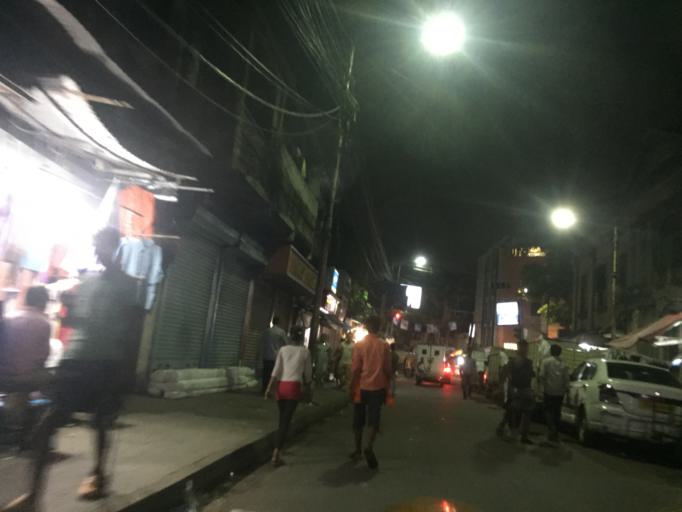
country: IN
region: West Bengal
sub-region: Kolkata
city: Bara Bazar
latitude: 22.5627
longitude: 88.3555
